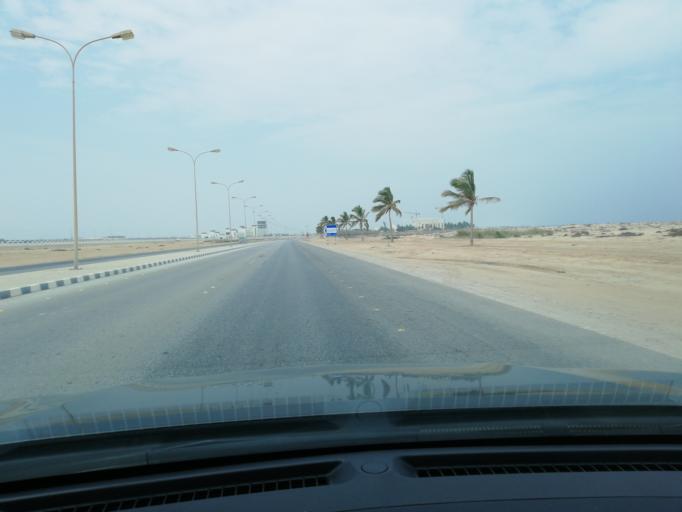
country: OM
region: Zufar
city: Salalah
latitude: 16.9764
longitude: 54.0071
